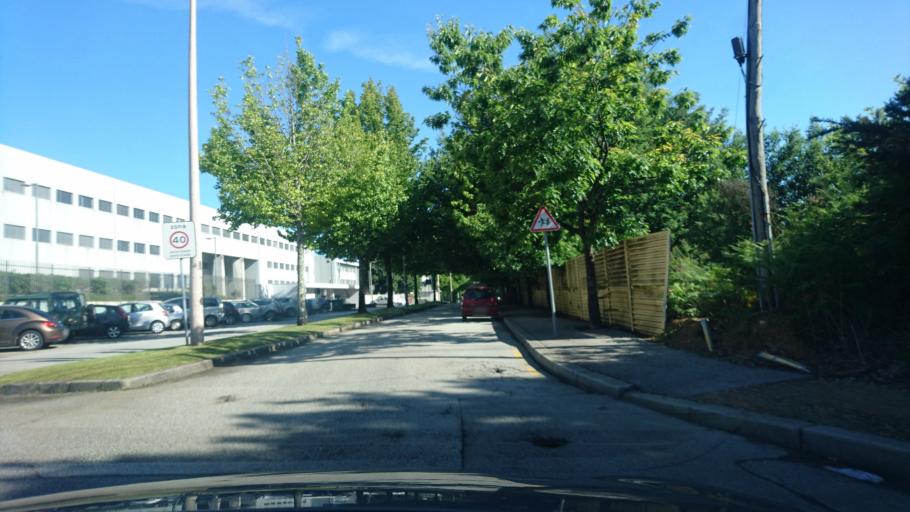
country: PT
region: Aveiro
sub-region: Sao Joao da Madeira
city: Sao Joao da Madeira
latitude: 40.8918
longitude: -8.4847
